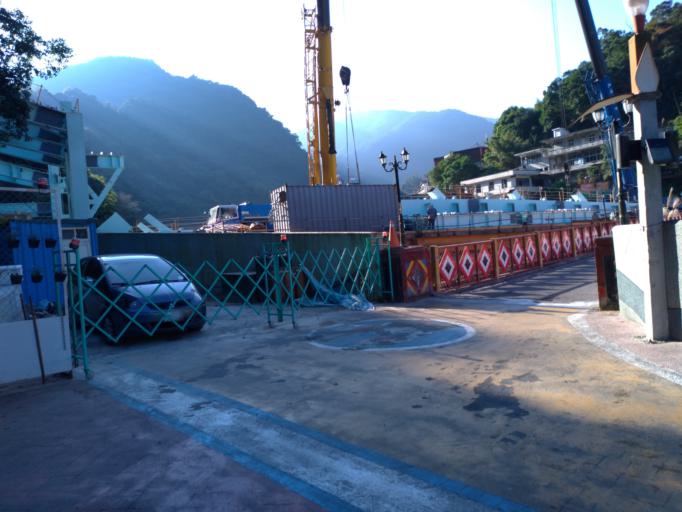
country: TW
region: Taipei
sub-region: Taipei
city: Banqiao
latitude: 24.8624
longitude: 121.5516
